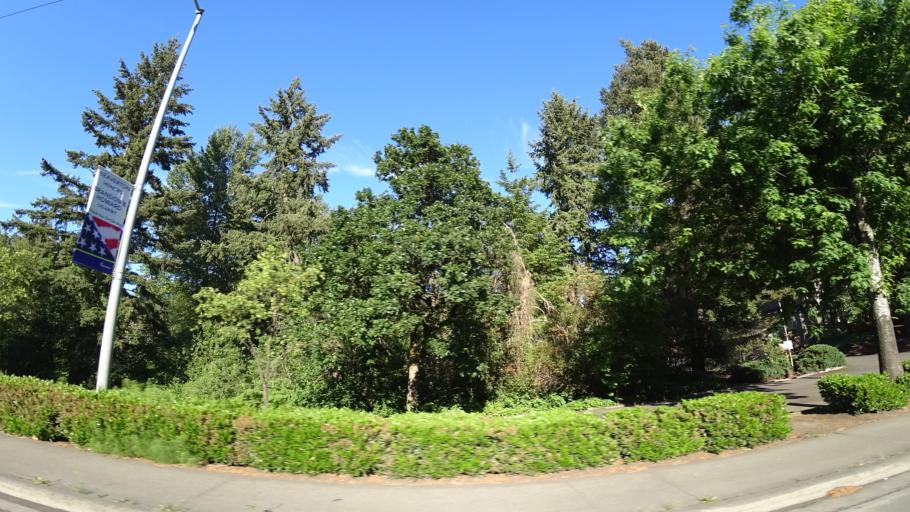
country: US
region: Oregon
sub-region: Washington County
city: Beaverton
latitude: 45.4686
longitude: -122.8260
